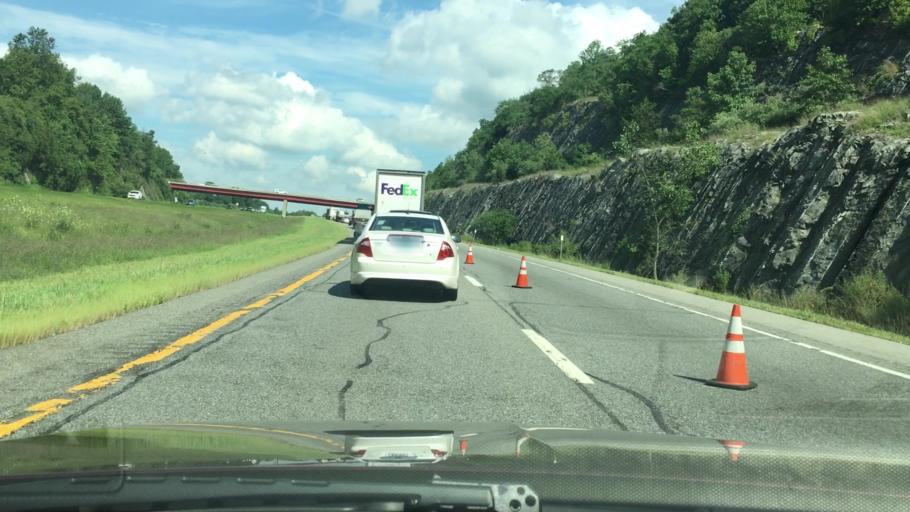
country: US
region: New York
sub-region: Putnam County
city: Brewster Hill
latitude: 41.4225
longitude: -73.6241
